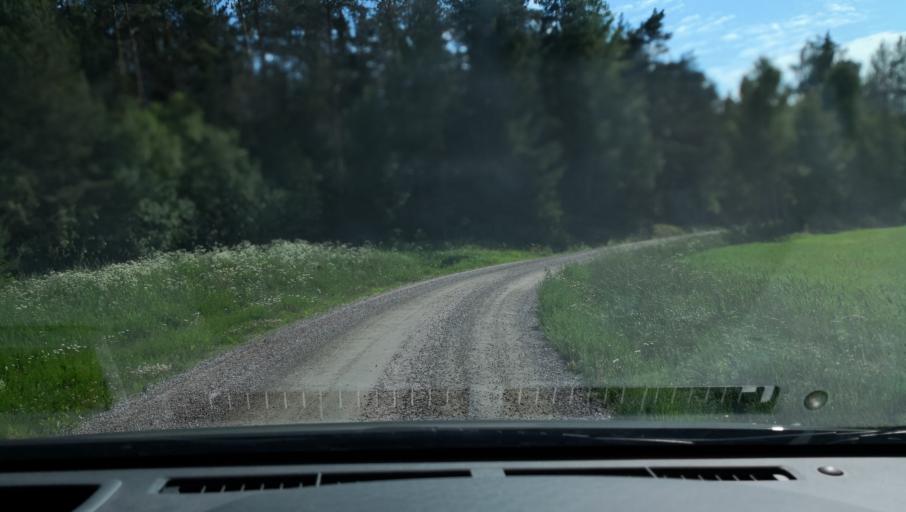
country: SE
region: Uppsala
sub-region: Enkopings Kommun
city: Orsundsbro
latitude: 59.8344
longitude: 17.2480
